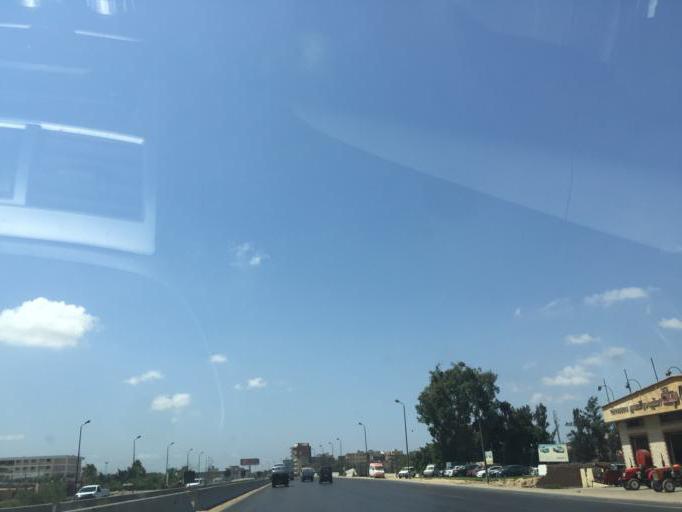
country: EG
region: Alexandria
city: Alexandria
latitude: 31.0007
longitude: 29.8072
